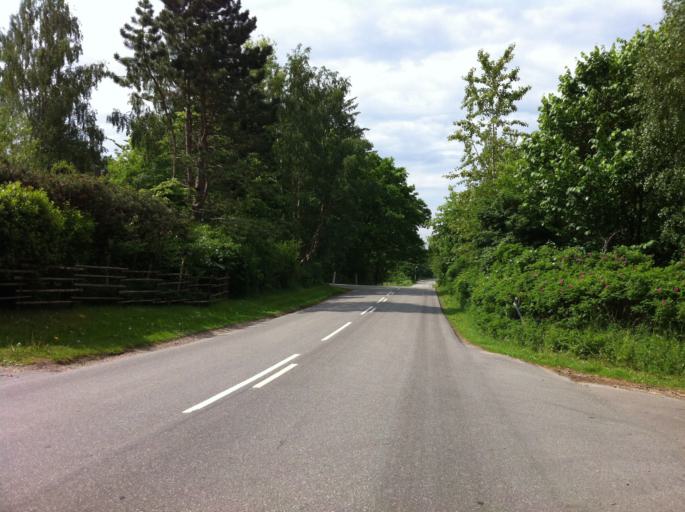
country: DK
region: Capital Region
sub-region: Gribskov Kommune
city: Helsinge
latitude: 56.1096
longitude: 12.1980
